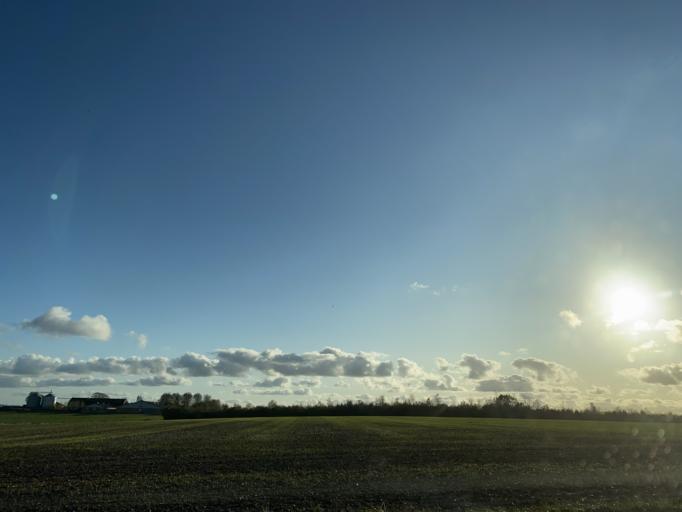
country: DK
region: Central Jutland
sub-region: Viborg Kommune
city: Bjerringbro
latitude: 56.3378
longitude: 9.7103
